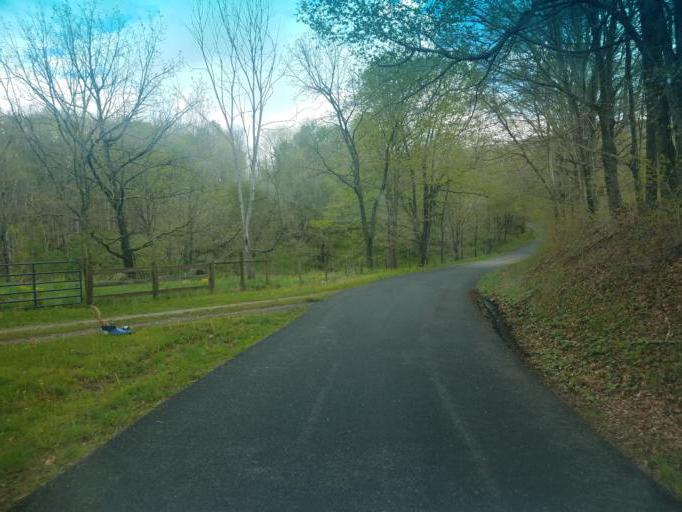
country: US
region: Virginia
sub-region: Smyth County
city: Atkins
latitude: 36.9558
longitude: -81.4007
